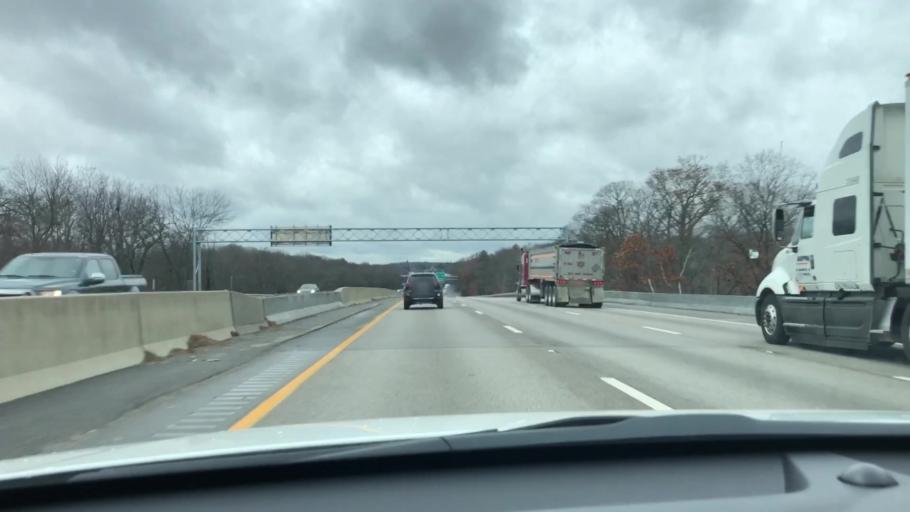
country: US
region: Massachusetts
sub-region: Norfolk County
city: Braintree
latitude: 42.2034
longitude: -70.9847
